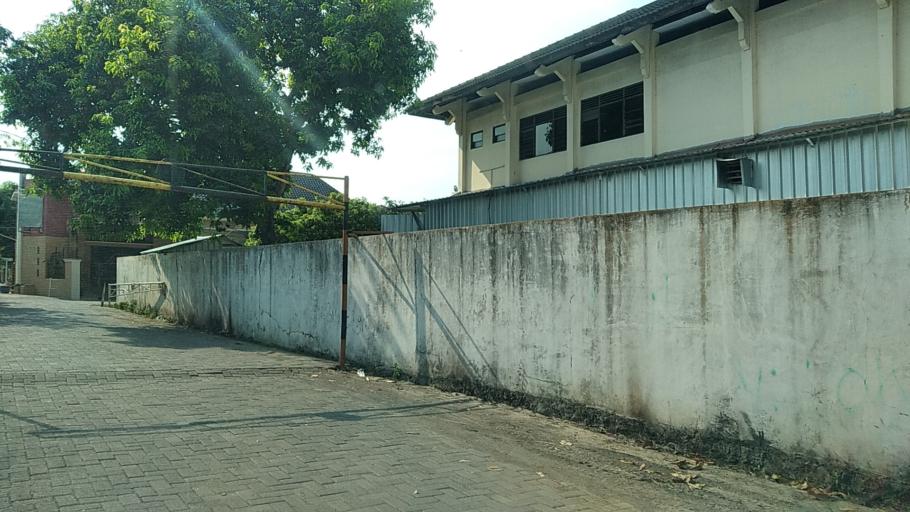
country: ID
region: Central Java
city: Semarang
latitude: -6.9975
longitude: 110.4556
